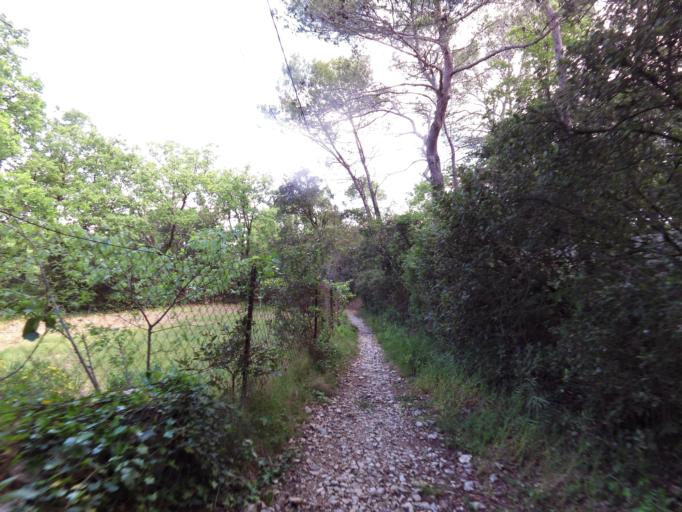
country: FR
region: Languedoc-Roussillon
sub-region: Departement du Gard
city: Aubais
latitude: 43.7593
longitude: 4.1482
